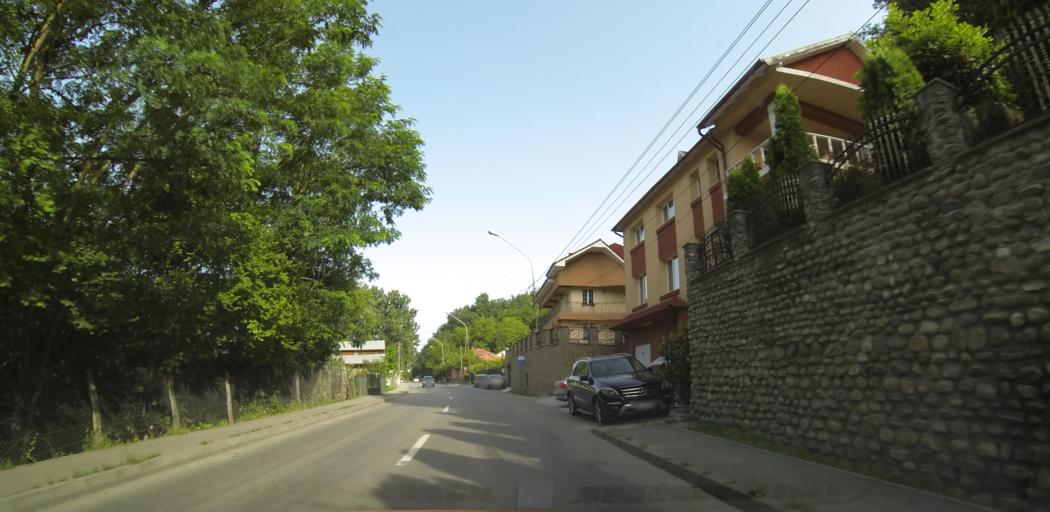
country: RO
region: Valcea
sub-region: Municipiul Ramnicu Valcea
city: Ramnicu Valcea
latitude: 45.1069
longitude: 24.3420
